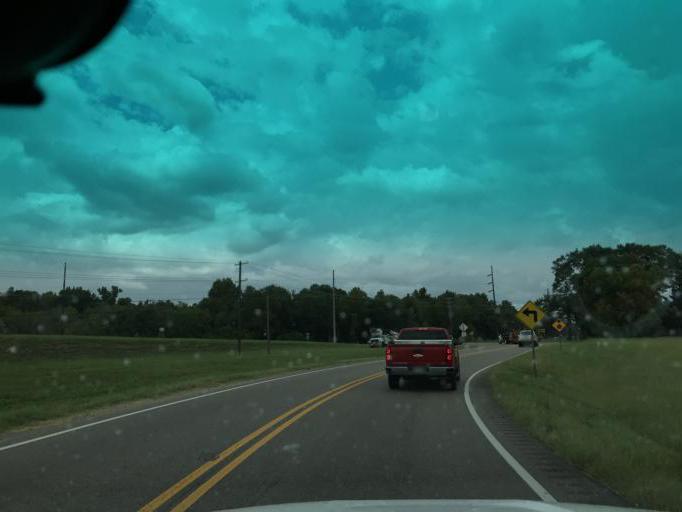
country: US
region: Alabama
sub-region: Montgomery County
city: Pike Road
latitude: 32.3670
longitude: -86.1017
